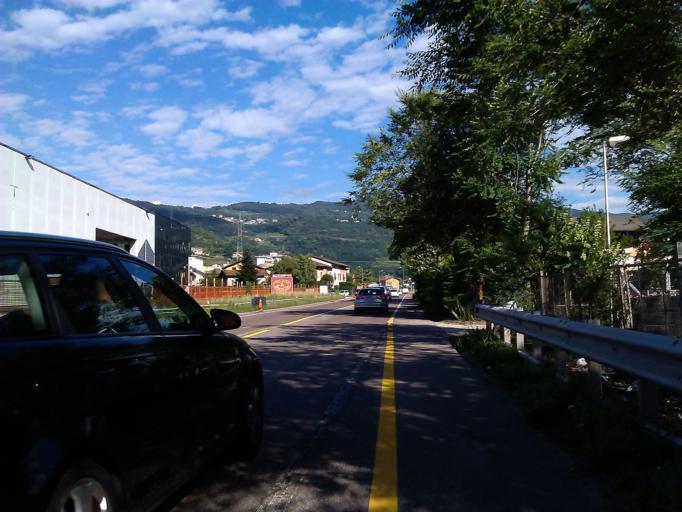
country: IT
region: Trentino-Alto Adige
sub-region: Provincia di Trento
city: Lavis
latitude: 46.1431
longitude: 11.1016
